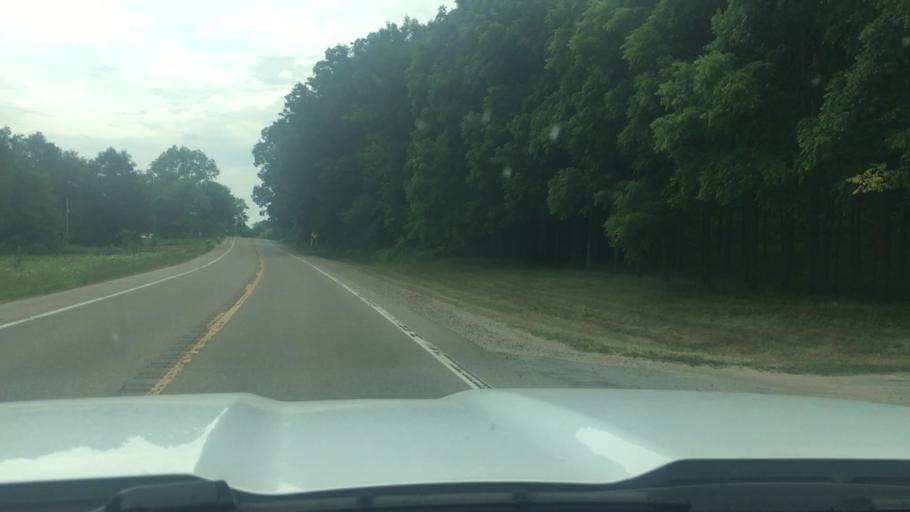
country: US
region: Michigan
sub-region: Ionia County
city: Saranac
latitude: 42.9344
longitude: -85.2660
